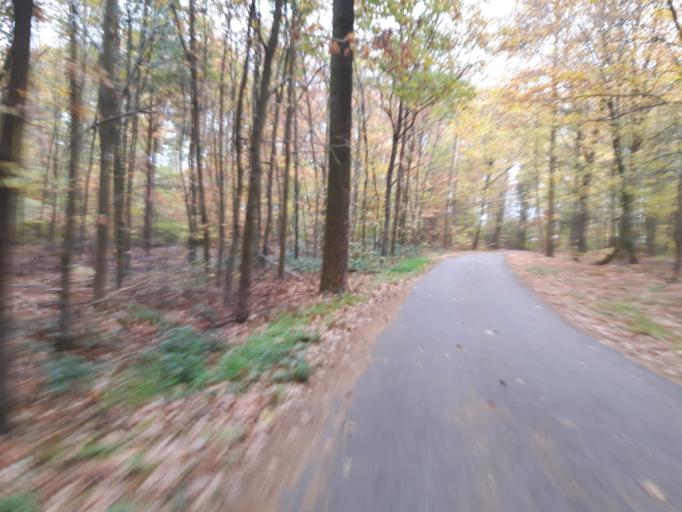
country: DE
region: Baden-Wuerttemberg
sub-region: Karlsruhe Region
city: Reilingen
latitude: 49.2851
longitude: 8.5813
